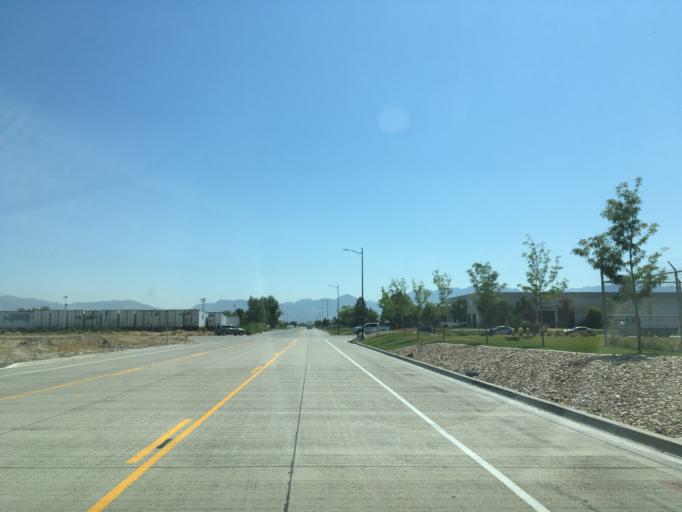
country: US
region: Utah
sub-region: Salt Lake County
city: West Valley City
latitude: 40.7183
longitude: -112.0206
